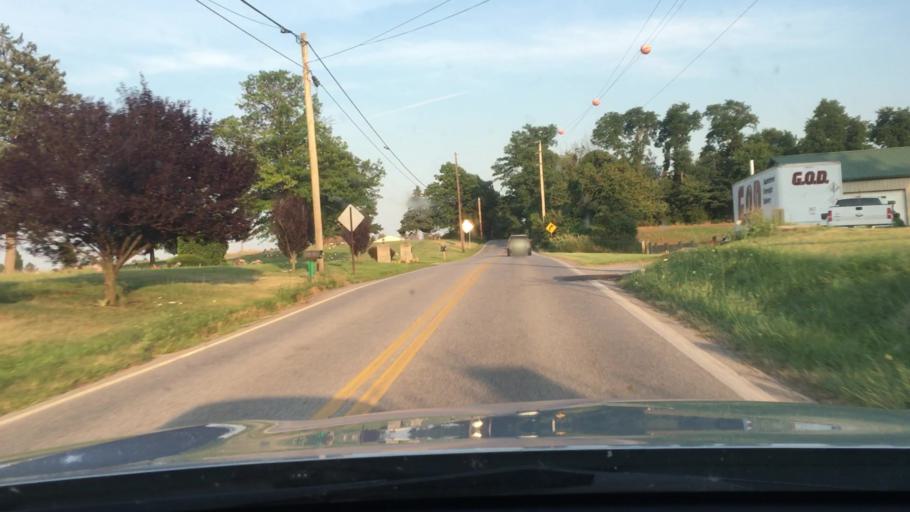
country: US
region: Pennsylvania
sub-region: York County
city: Weigelstown
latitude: 40.0202
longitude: -76.8176
